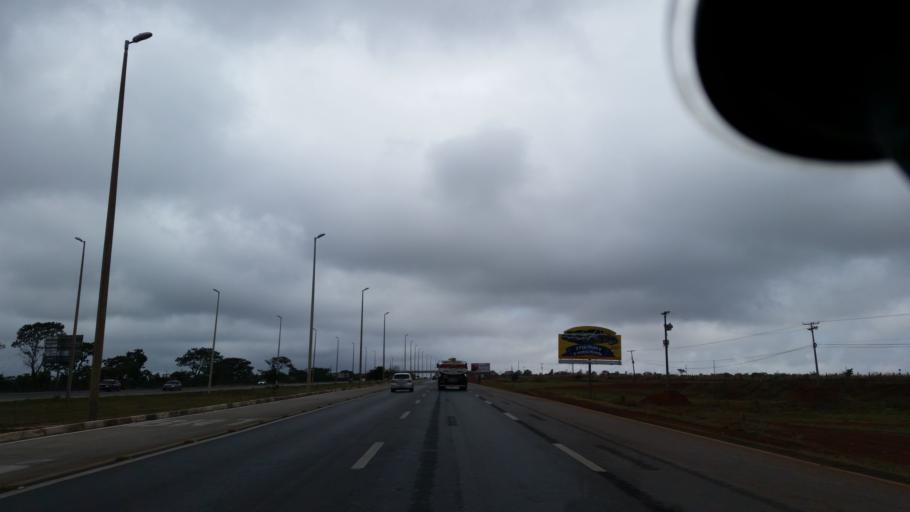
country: BR
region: Federal District
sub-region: Brasilia
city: Brasilia
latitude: -15.9666
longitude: -47.9921
